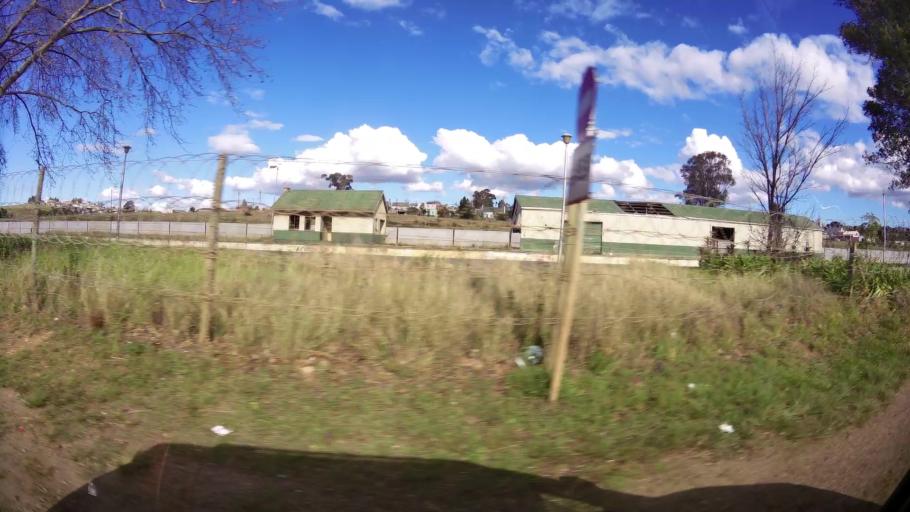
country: ZA
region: Western Cape
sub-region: Overberg District Municipality
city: Swellendam
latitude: -34.0296
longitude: 20.4442
